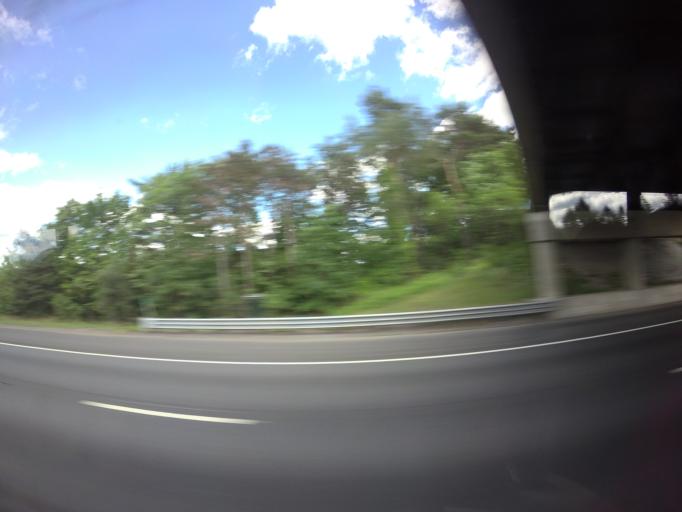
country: US
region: Massachusetts
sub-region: Middlesex County
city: Wilmington
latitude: 42.5333
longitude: -71.1354
